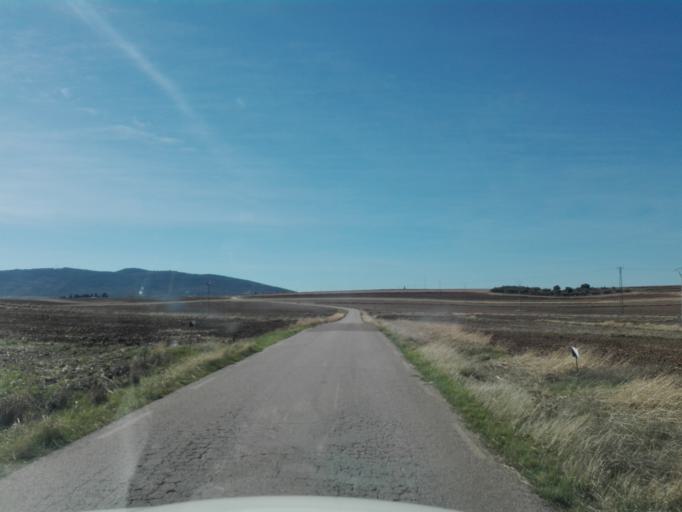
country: ES
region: Extremadura
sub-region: Provincia de Badajoz
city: Llerena
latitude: 38.2554
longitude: -5.9950
